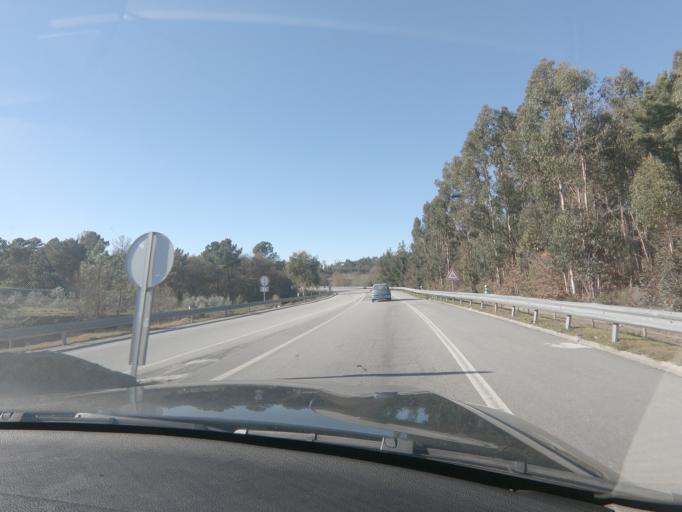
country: PT
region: Viseu
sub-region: Viseu
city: Abraveses
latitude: 40.6745
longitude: -7.9765
